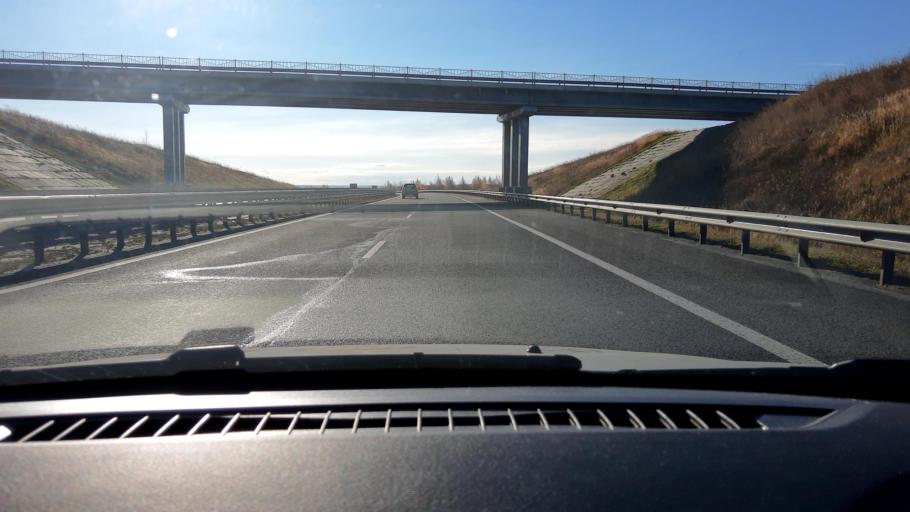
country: RU
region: Nizjnij Novgorod
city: Burevestnik
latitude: 56.1523
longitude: 43.7491
